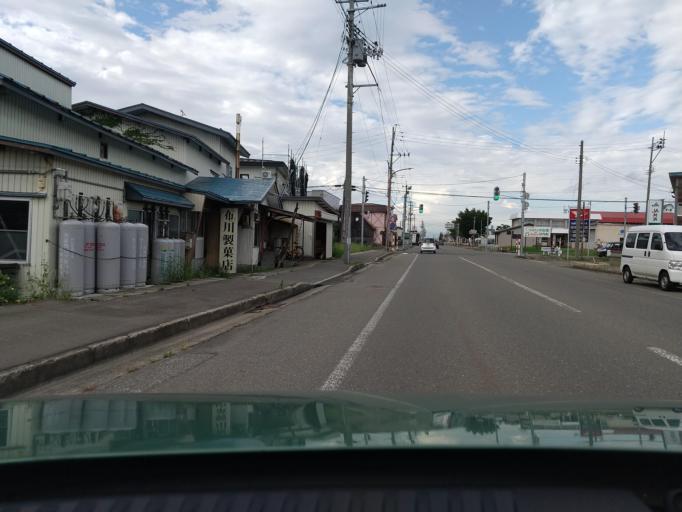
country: JP
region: Akita
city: Yokotemachi
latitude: 39.2614
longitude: 140.4904
